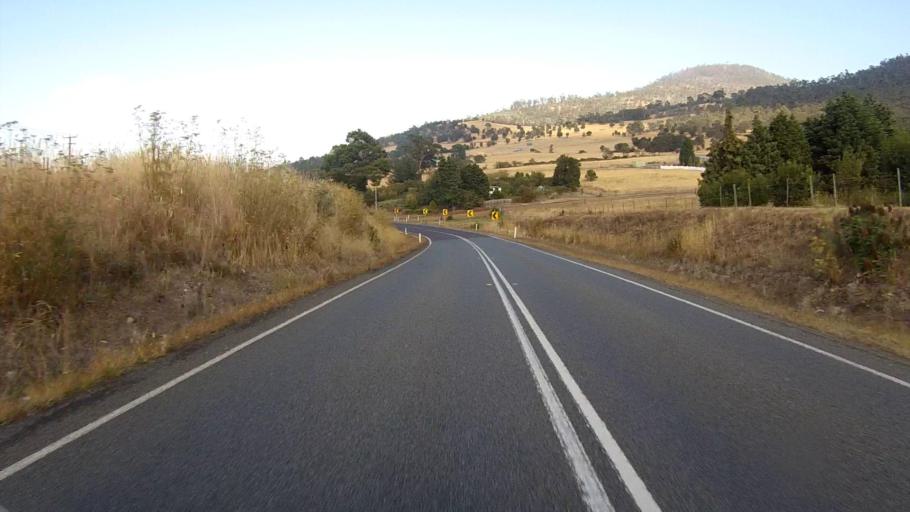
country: AU
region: Tasmania
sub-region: Glenorchy
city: Granton
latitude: -42.7489
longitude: 147.1544
